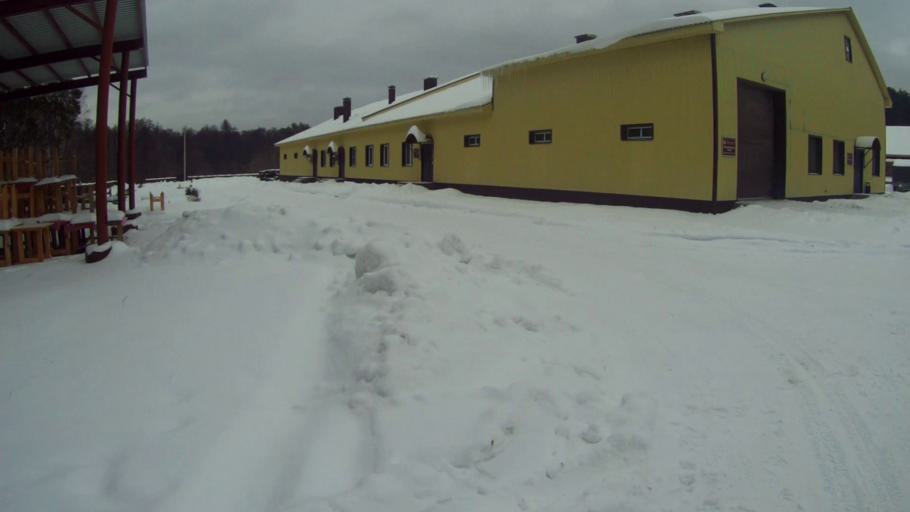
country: RU
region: Mordoviya
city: Sosnovka
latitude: 54.7129
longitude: 43.2243
